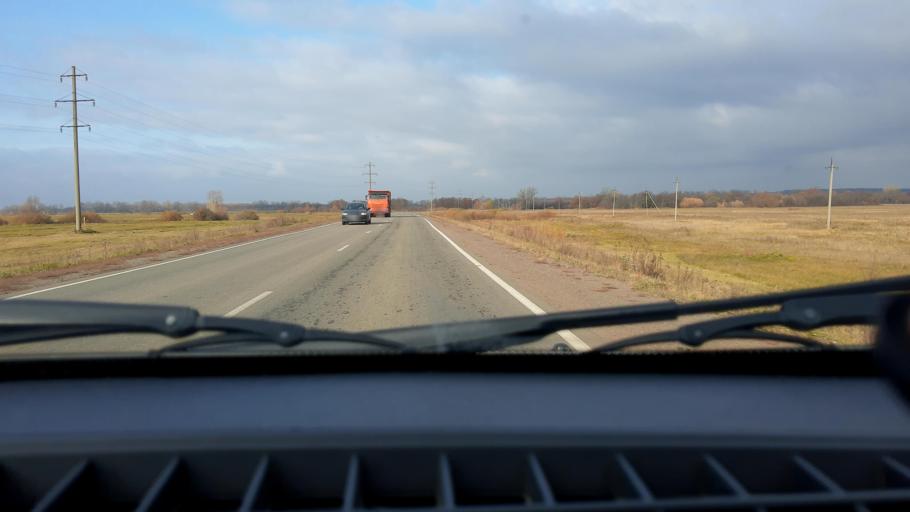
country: RU
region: Bashkortostan
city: Kabakovo
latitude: 54.5601
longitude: 56.0061
